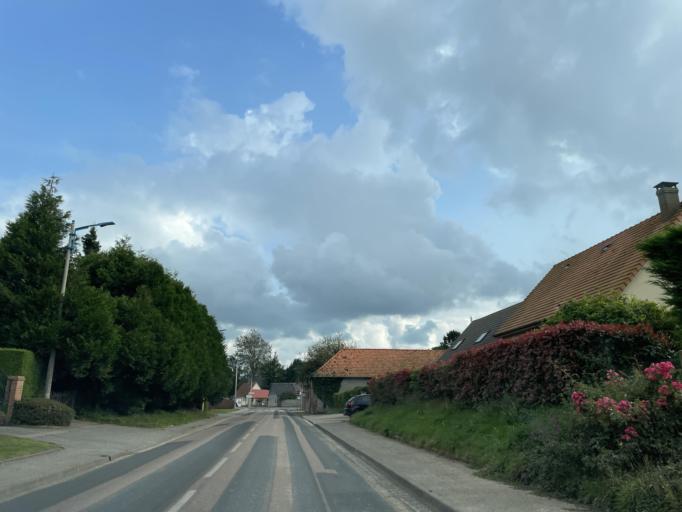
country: FR
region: Haute-Normandie
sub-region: Departement de la Seine-Maritime
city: Envermeu
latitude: 49.9326
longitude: 1.2762
